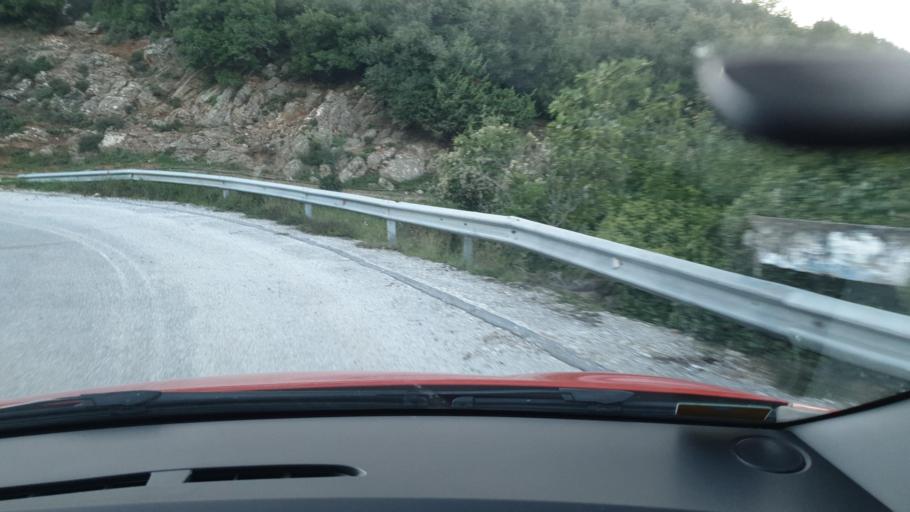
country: GR
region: Central Macedonia
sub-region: Nomos Chalkidikis
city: Galatista
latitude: 40.4626
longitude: 23.3221
